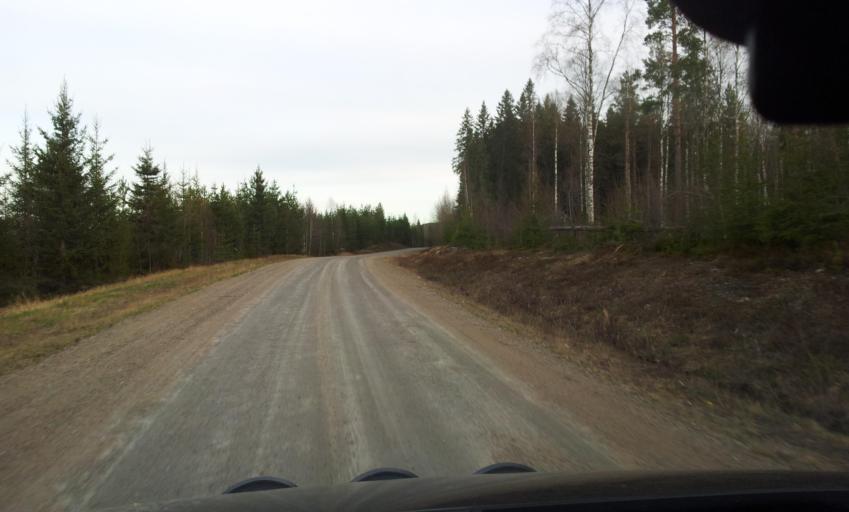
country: SE
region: Gaevleborg
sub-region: Ljusdals Kommun
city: Farila
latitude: 62.0850
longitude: 15.7695
